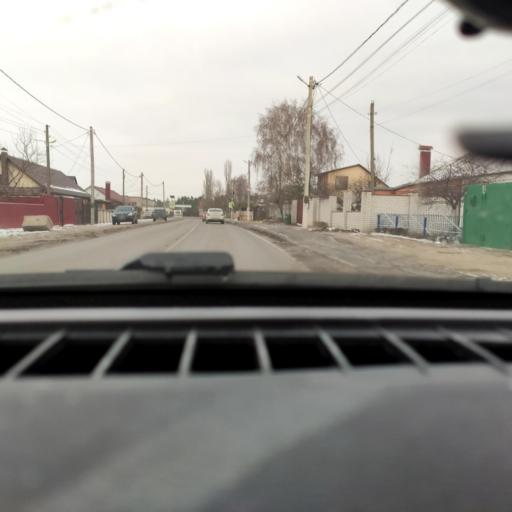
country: RU
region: Voronezj
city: Podgornoye
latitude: 51.7951
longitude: 39.1476
